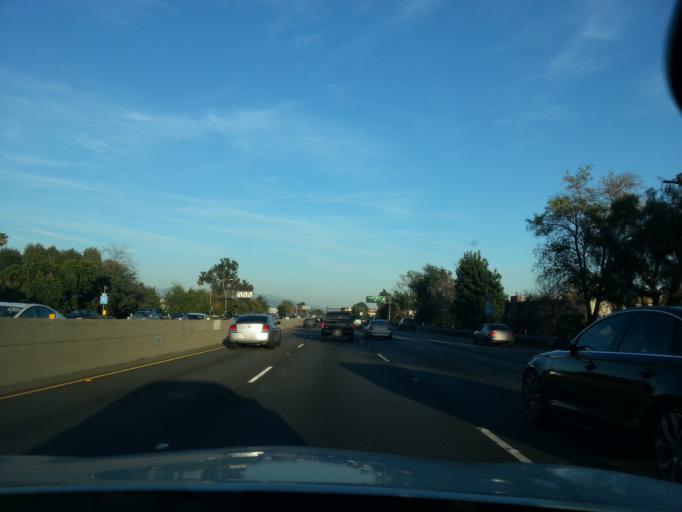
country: US
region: California
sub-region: Los Angeles County
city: Northridge
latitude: 34.1711
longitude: -118.5237
